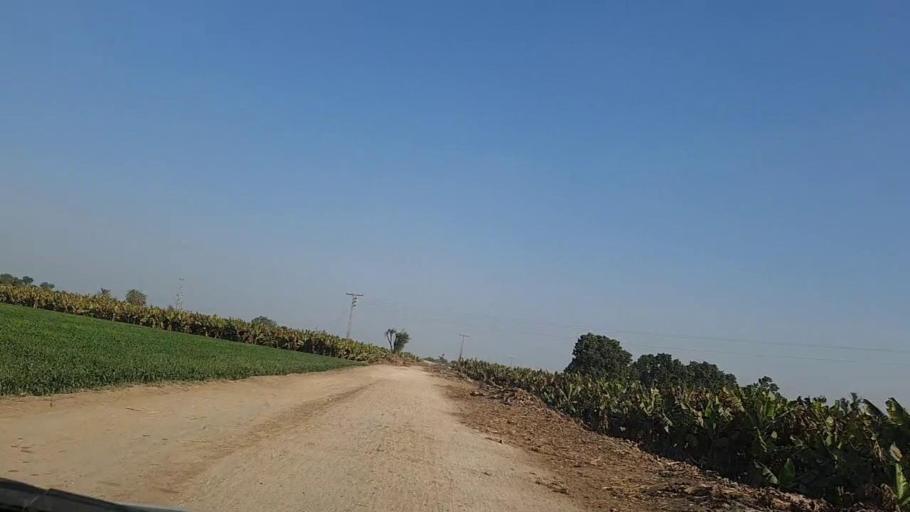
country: PK
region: Sindh
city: Sakrand
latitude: 26.0212
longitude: 68.3250
